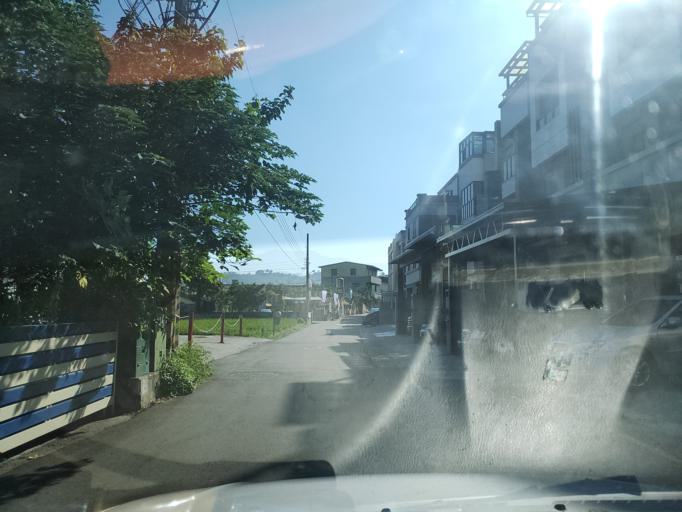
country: TW
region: Taiwan
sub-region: Miaoli
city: Miaoli
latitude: 24.5619
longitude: 120.8299
